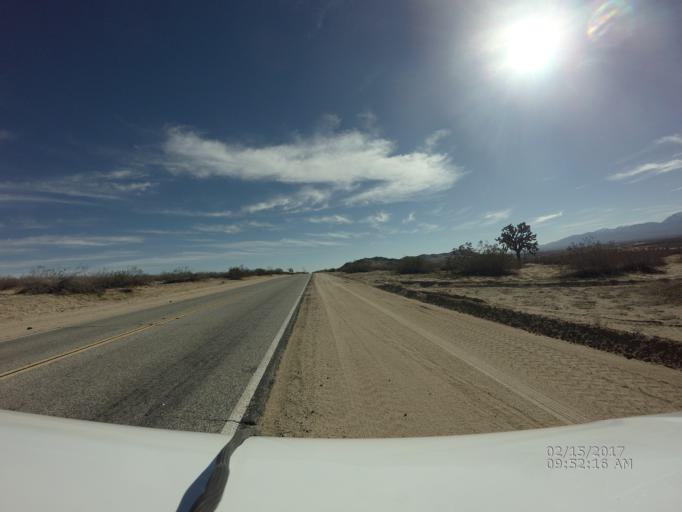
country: US
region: California
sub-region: Los Angeles County
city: Lake Los Angeles
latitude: 34.6166
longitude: -117.9040
